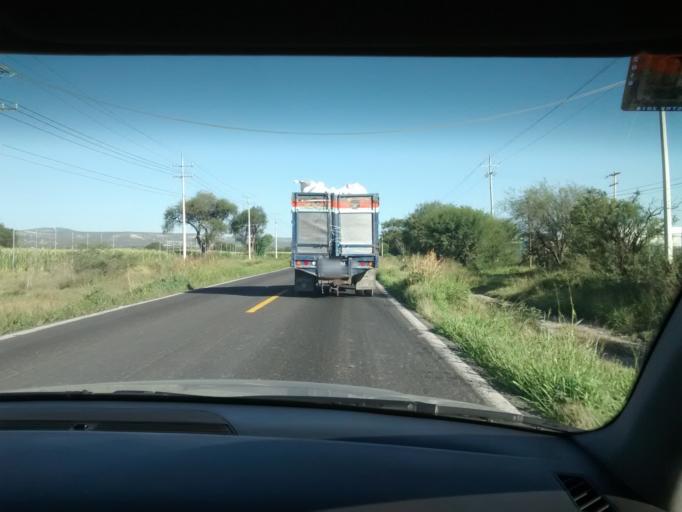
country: MX
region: Puebla
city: San Bartolo Teontepec
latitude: 18.5409
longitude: -97.5371
